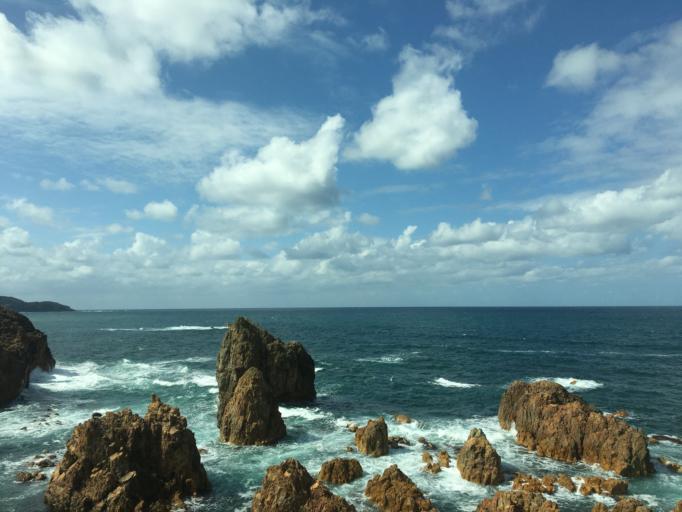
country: JP
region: Aomori
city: Shimokizukuri
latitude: 40.6620
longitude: 139.9375
